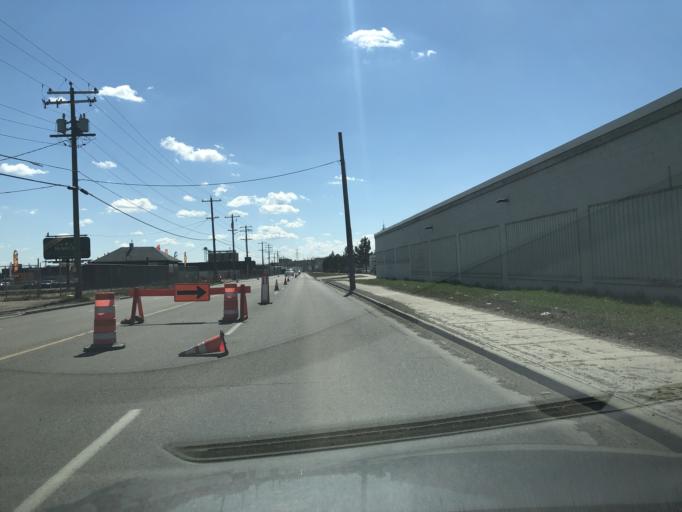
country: CA
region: Alberta
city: Calgary
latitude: 51.0280
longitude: -114.0310
